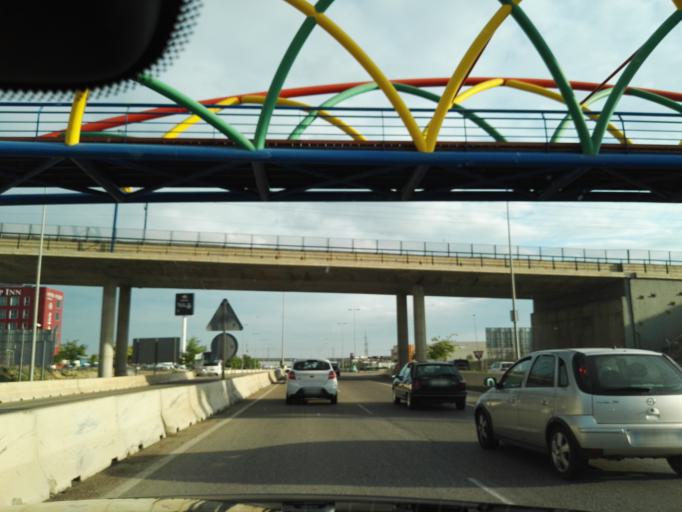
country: ES
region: Aragon
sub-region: Provincia de Zaragoza
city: Montecanal
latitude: 41.6339
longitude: -0.9892
